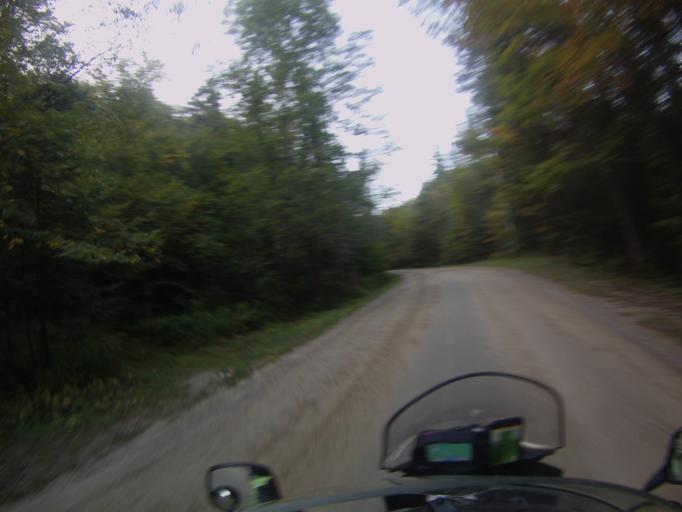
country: US
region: Vermont
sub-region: Addison County
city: Bristol
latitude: 44.0160
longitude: -73.0215
